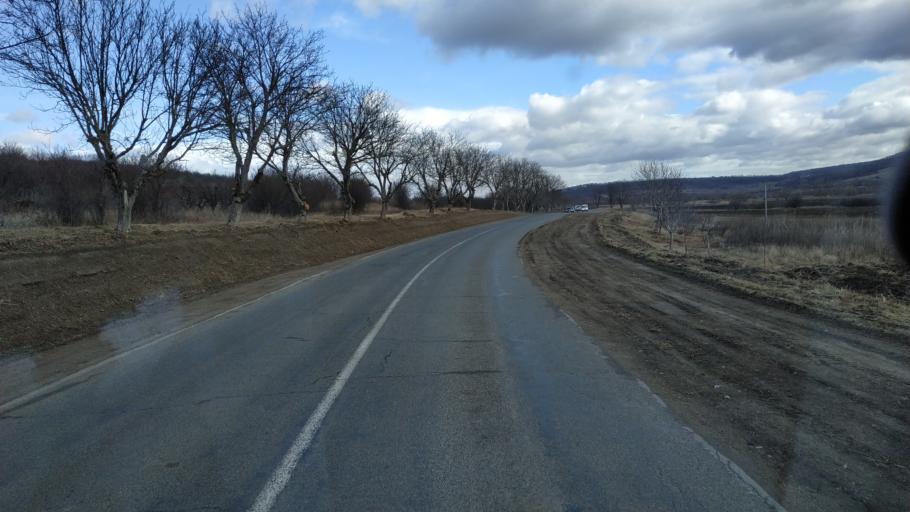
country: MD
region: Stinga Nistrului
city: Bucovat
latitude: 47.1696
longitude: 28.4417
